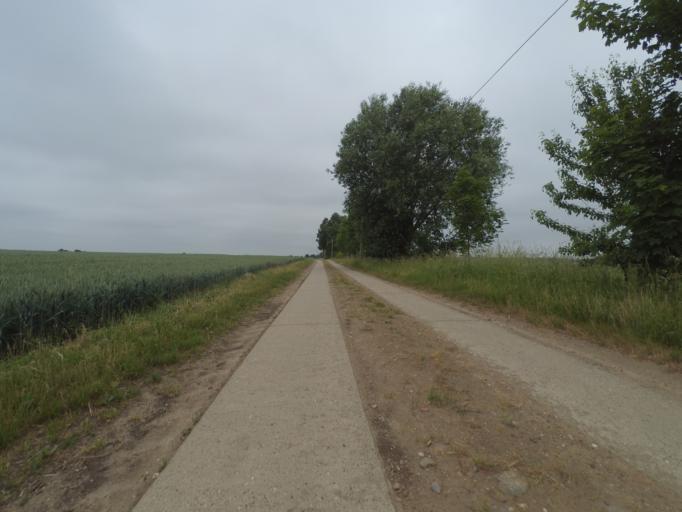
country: DE
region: Mecklenburg-Vorpommern
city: Dabel
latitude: 53.6684
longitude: 11.9334
